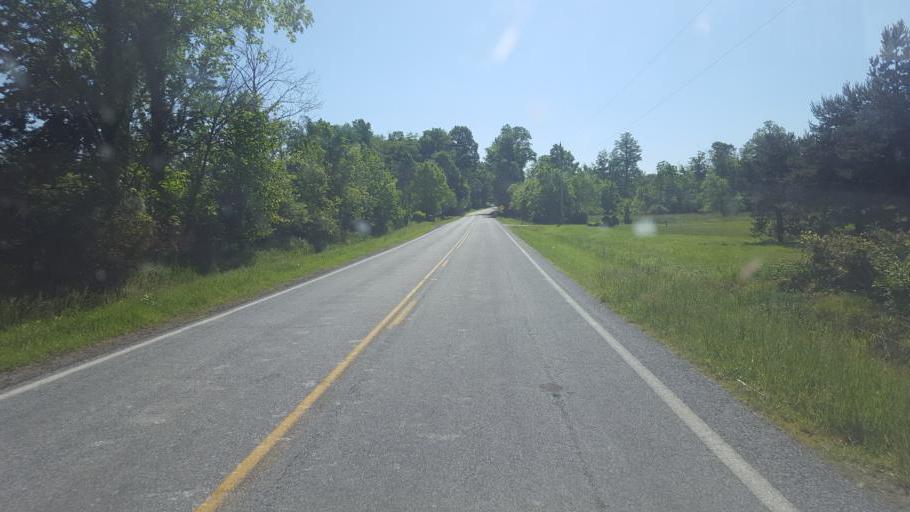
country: US
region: Ohio
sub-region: Crawford County
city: Crestline
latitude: 40.7695
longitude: -82.6904
